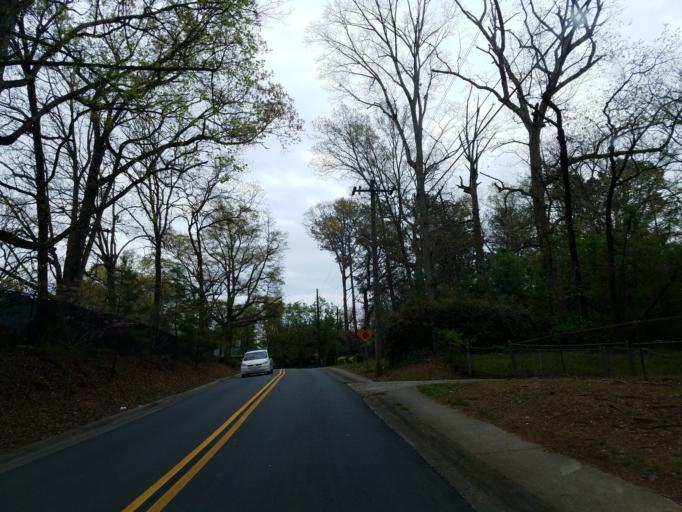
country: US
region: Georgia
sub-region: Cobb County
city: Fair Oaks
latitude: 33.8895
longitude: -84.5411
